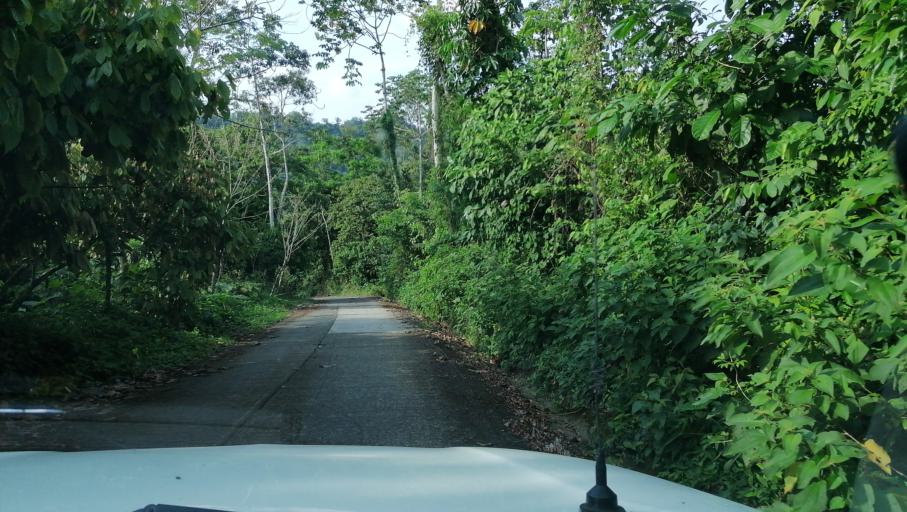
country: MX
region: Chiapas
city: Ostuacan
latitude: 17.4703
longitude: -93.2348
